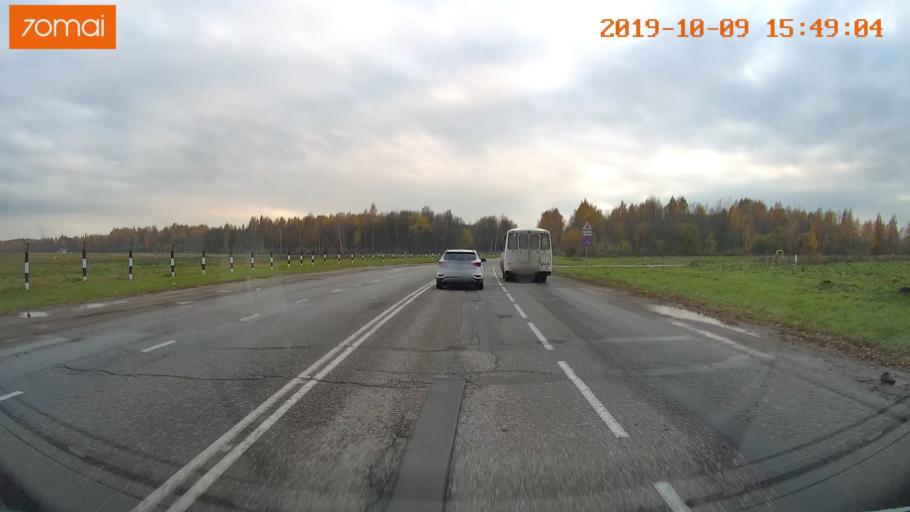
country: RU
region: Kostroma
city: Oktyabr'skiy
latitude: 57.8075
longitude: 41.0089
